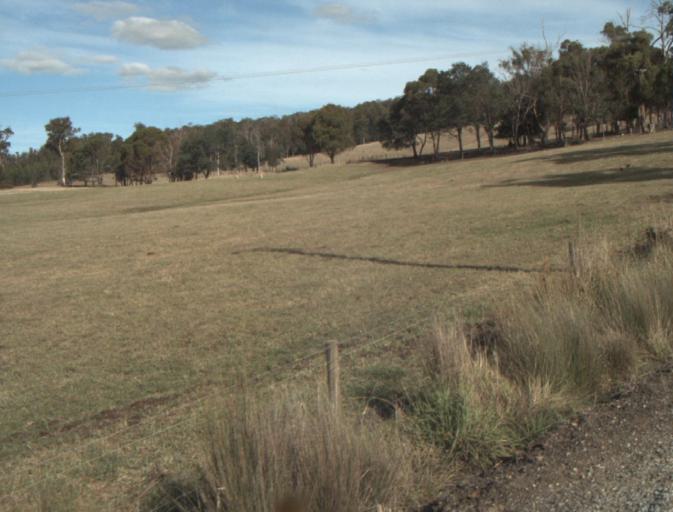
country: AU
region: Tasmania
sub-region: Launceston
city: Mayfield
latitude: -41.2203
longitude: 147.1582
